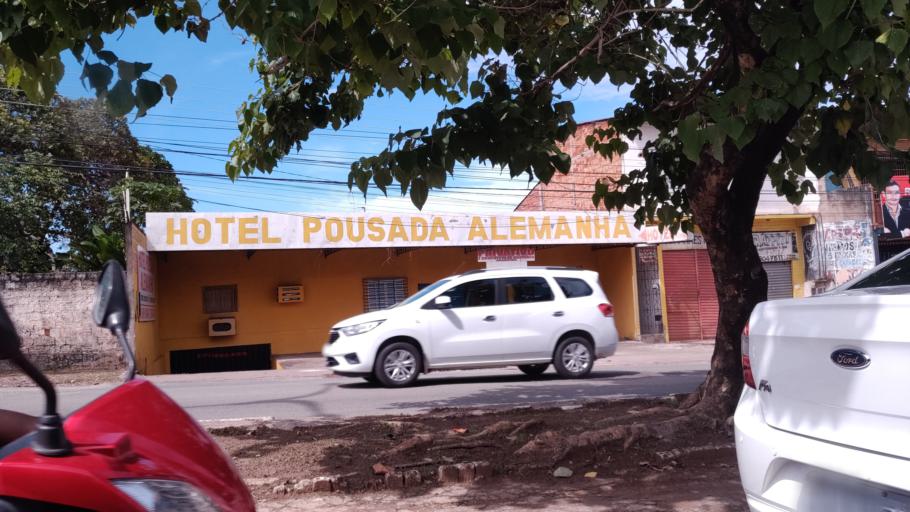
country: BR
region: Maranhao
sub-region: Sao Luis
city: Sao Luis
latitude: -2.5390
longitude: -44.2675
